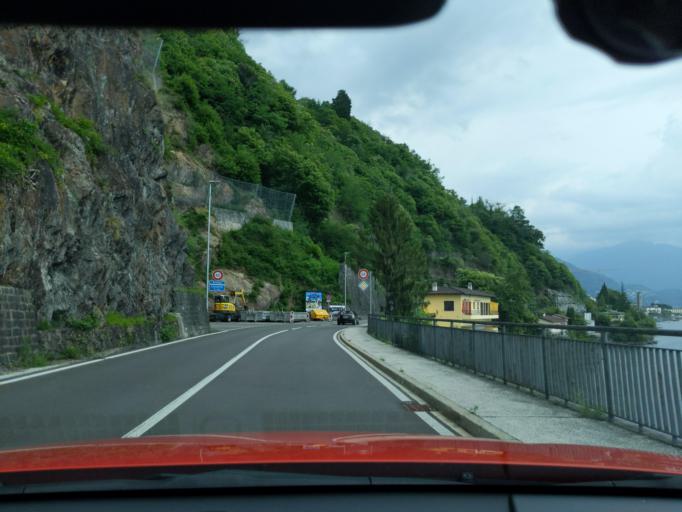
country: CH
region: Ticino
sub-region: Locarno District
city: Brissago
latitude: 46.1032
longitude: 8.6972
